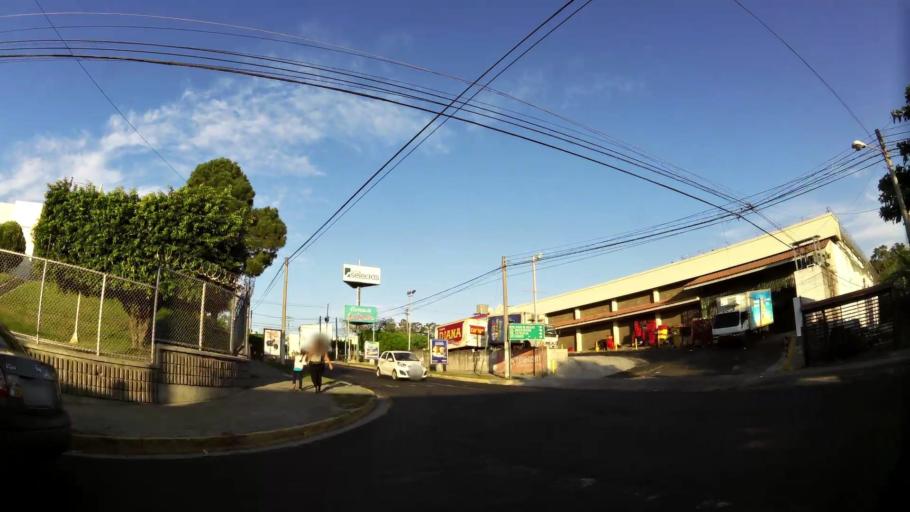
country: SV
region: La Libertad
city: Santa Tecla
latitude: 13.6802
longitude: -89.2626
